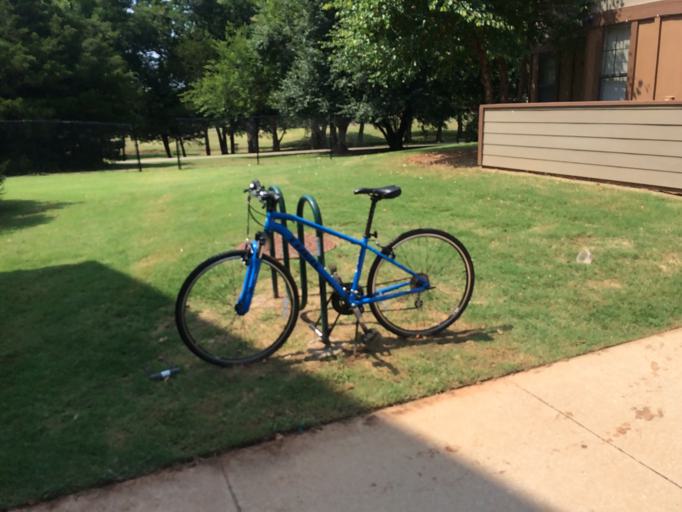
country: US
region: Oklahoma
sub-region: Cleveland County
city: Norman
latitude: 35.2052
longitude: -97.4167
